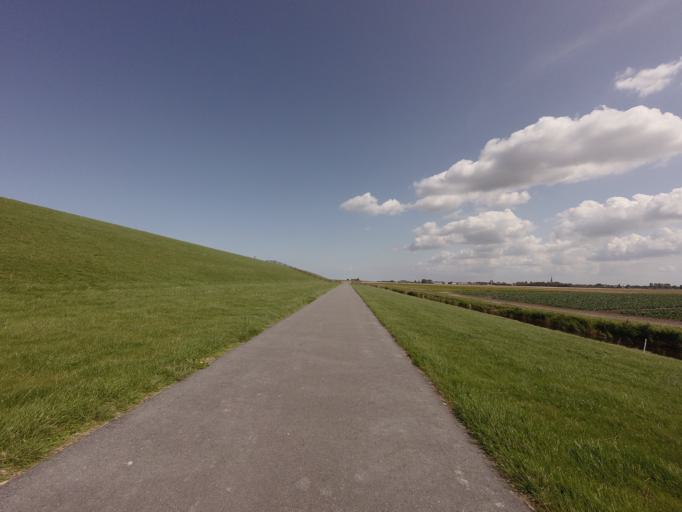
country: NL
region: Friesland
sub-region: Gemeente Dongeradeel
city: Holwerd
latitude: 53.3737
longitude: 5.8725
